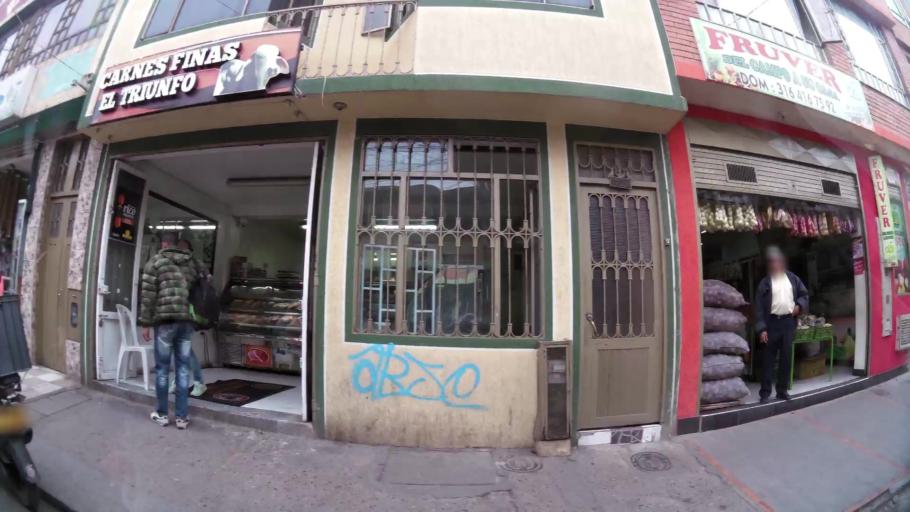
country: CO
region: Cundinamarca
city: Funza
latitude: 4.7108
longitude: -74.2188
